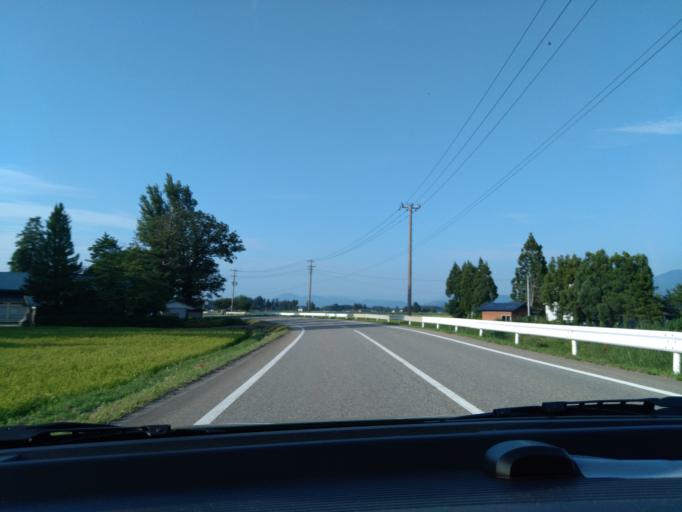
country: JP
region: Akita
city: Kakunodatemachi
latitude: 39.5277
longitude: 140.5583
